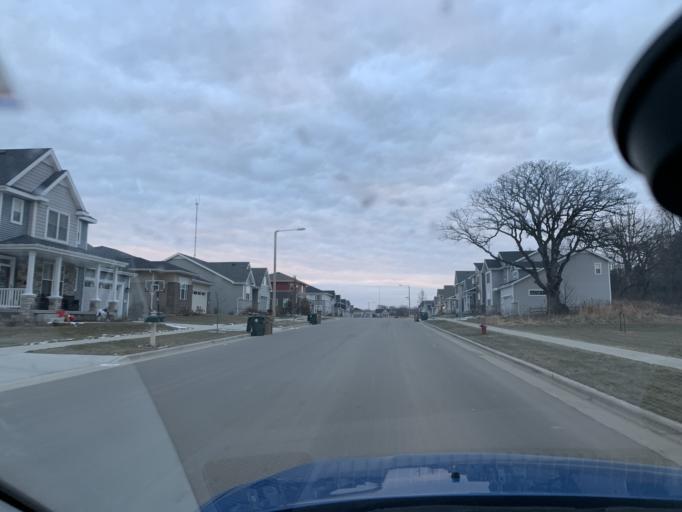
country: US
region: Wisconsin
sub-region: Dane County
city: Verona
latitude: 43.0495
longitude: -89.5568
